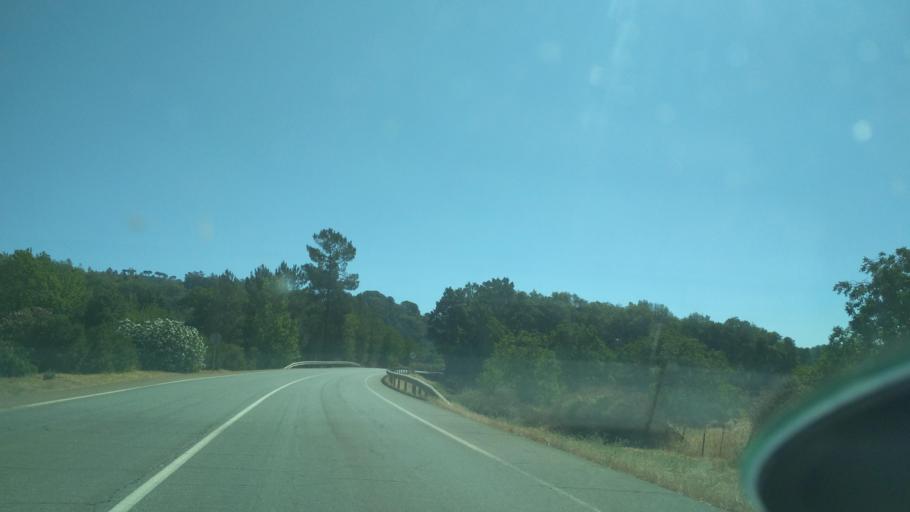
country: ES
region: Andalusia
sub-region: Provincia de Huelva
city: Galaroza
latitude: 37.9210
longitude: -6.7021
